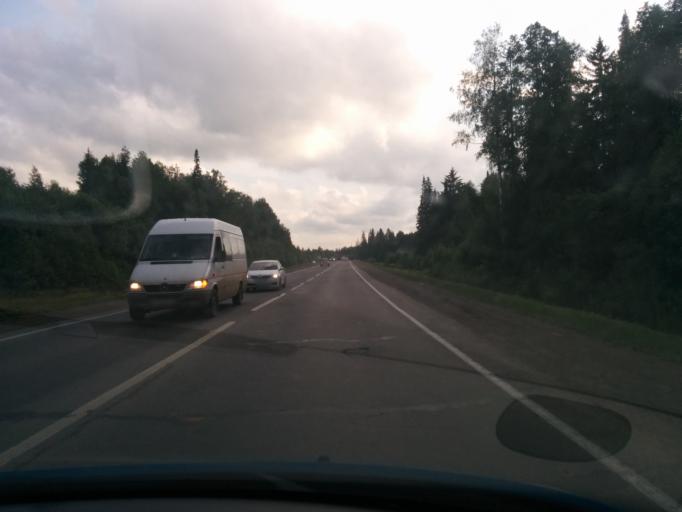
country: RU
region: Perm
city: Novyye Lyady
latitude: 58.0674
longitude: 56.4300
